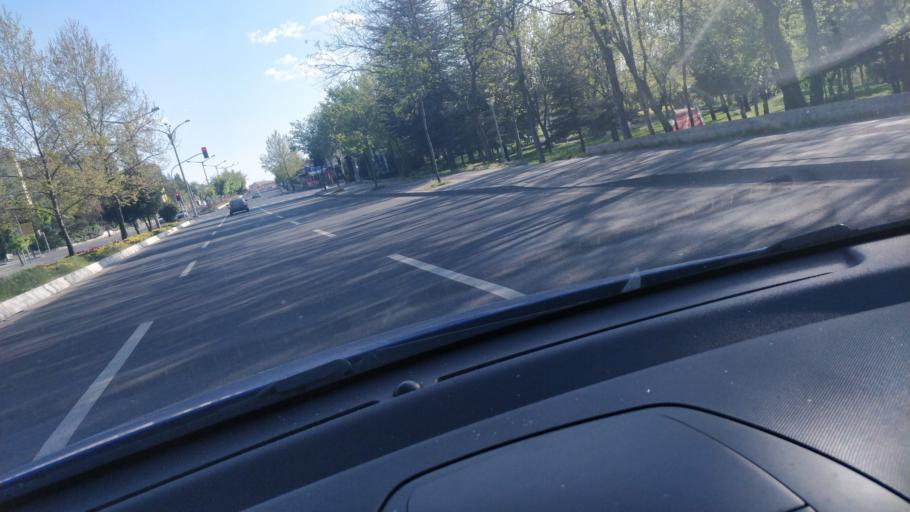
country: TR
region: Ankara
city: Batikent
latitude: 39.9626
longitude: 32.7327
